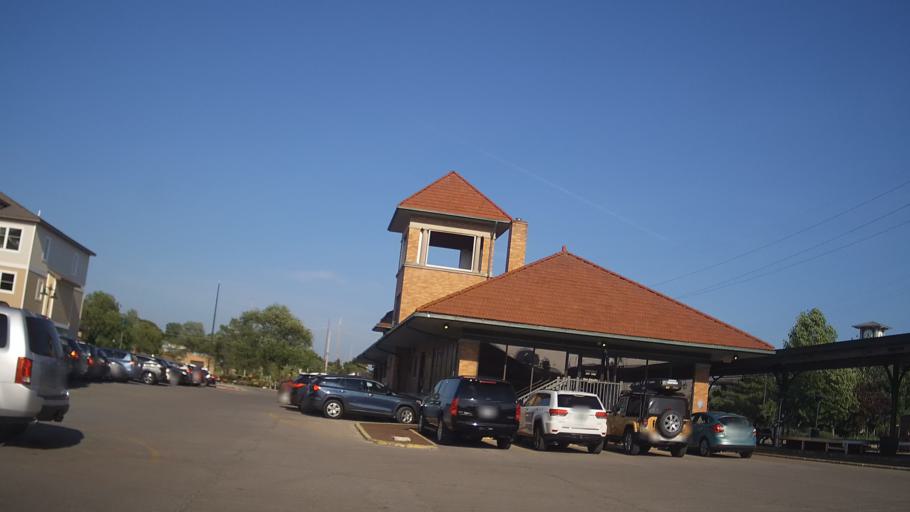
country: US
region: Michigan
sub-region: Grand Traverse County
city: Traverse City
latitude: 44.7583
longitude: -85.6100
